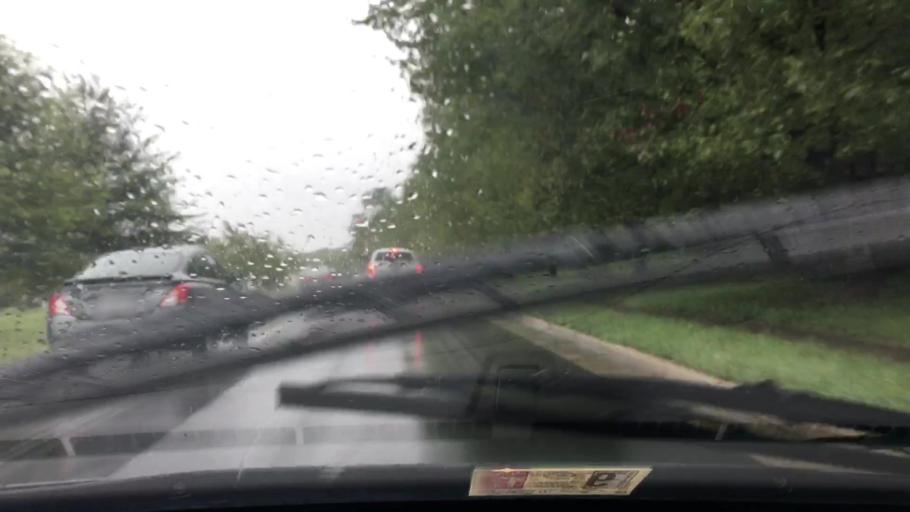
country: US
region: Virginia
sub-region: Loudoun County
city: Oak Grove
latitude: 39.0050
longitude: -77.3990
